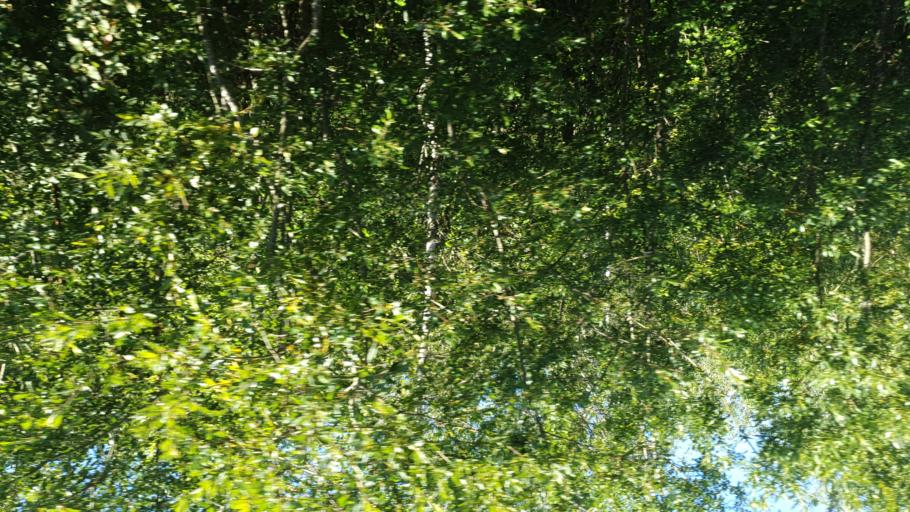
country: NO
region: Sor-Trondelag
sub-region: Orkdal
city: Orkanger
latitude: 63.1953
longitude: 9.7865
